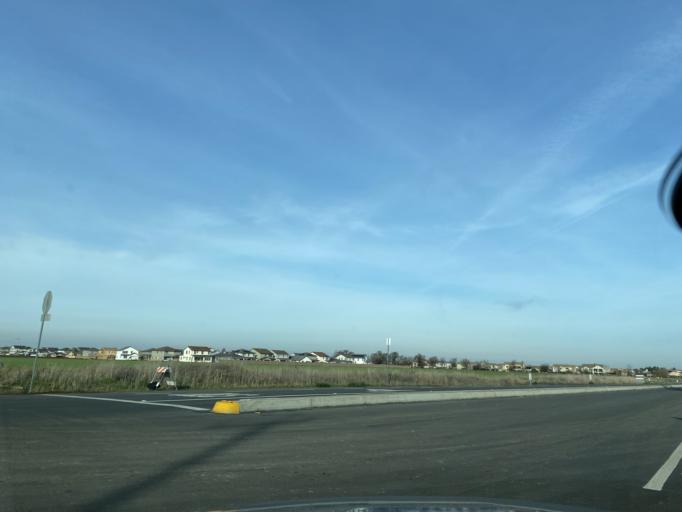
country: US
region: California
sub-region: Sacramento County
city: Elk Grove
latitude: 38.3909
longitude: -121.3991
